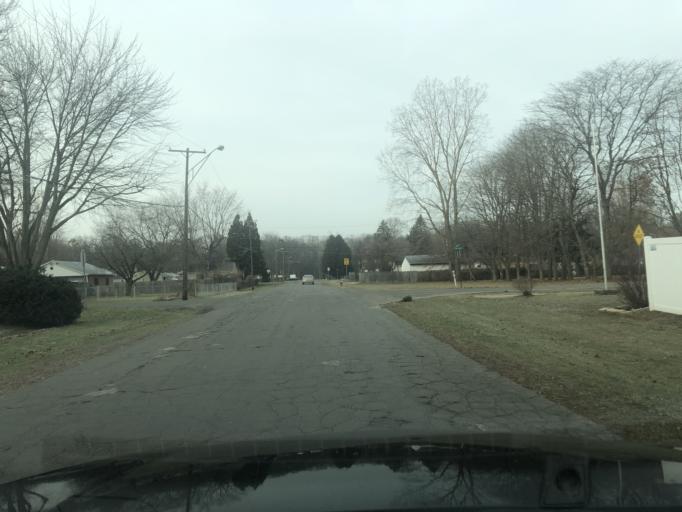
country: US
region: Michigan
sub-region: Wayne County
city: Romulus
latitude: 42.1858
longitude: -83.3264
